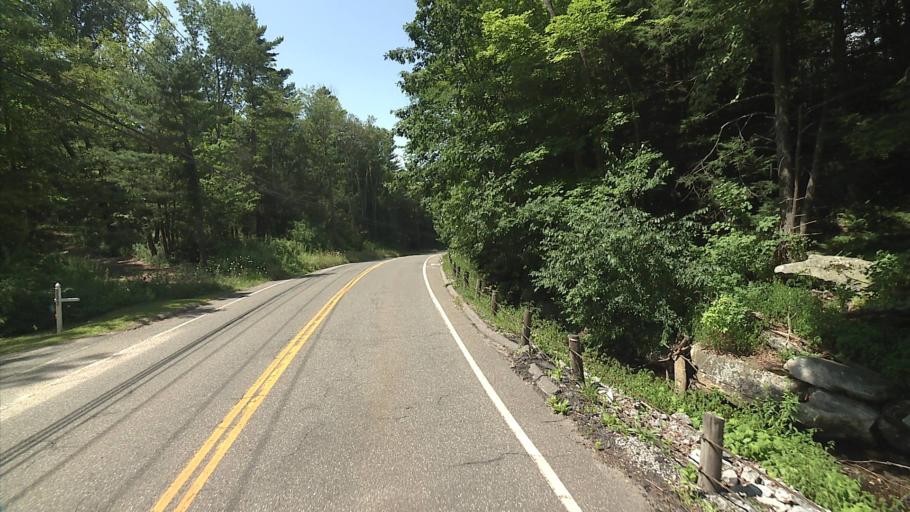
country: US
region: Connecticut
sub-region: Litchfield County
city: Canaan
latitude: 41.8718
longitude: -73.3332
